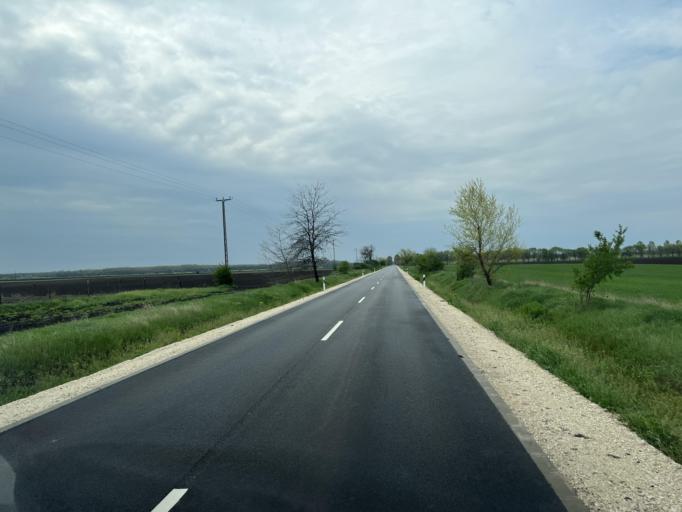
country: HU
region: Pest
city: Nyaregyhaza
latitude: 47.2449
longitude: 19.5208
